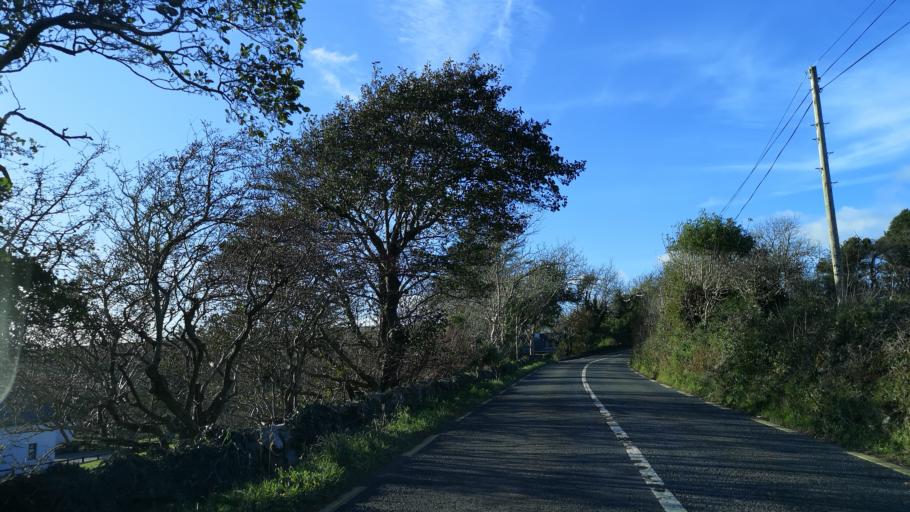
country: IE
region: Connaught
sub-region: County Galway
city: Clifden
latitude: 53.5409
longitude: -10.0101
